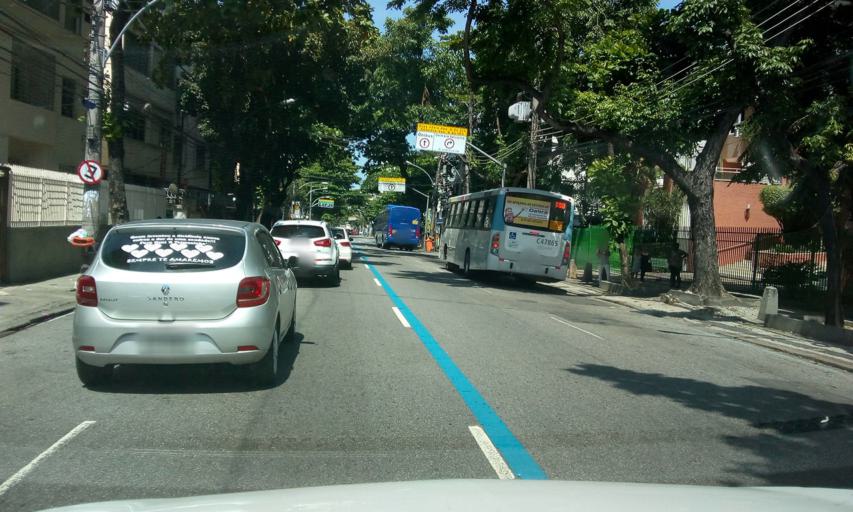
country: BR
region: Rio de Janeiro
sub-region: Rio De Janeiro
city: Rio de Janeiro
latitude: -22.9202
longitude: -43.2587
